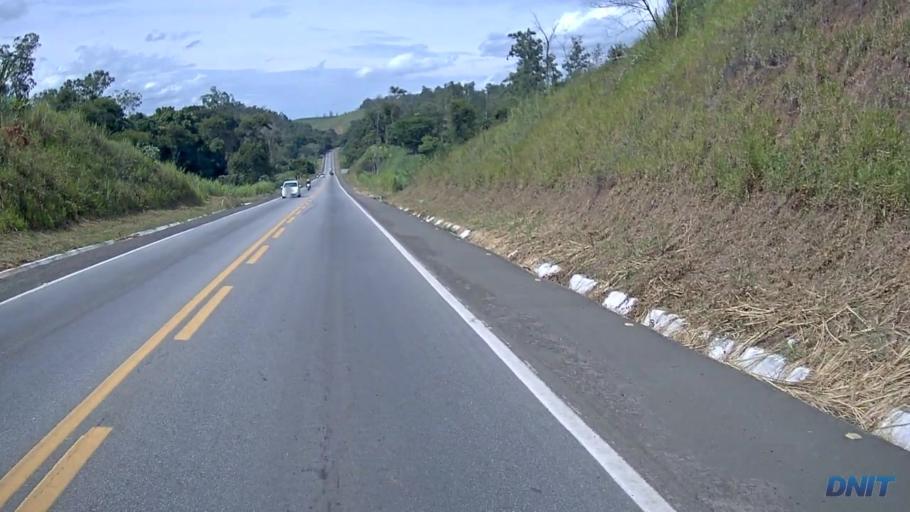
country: BR
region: Minas Gerais
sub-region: Ipatinga
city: Ipatinga
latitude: -19.4329
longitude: -42.5069
